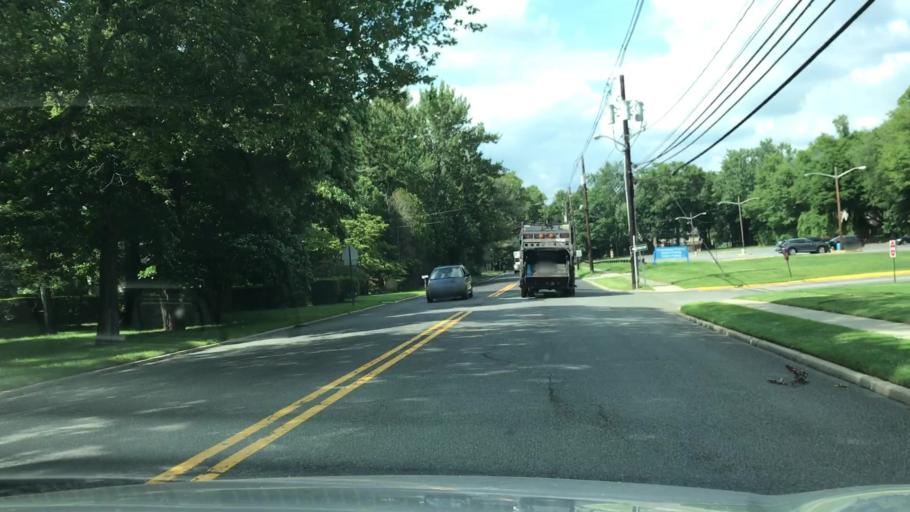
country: US
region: New Jersey
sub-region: Bergen County
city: Demarest
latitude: 40.9641
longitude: -73.9744
